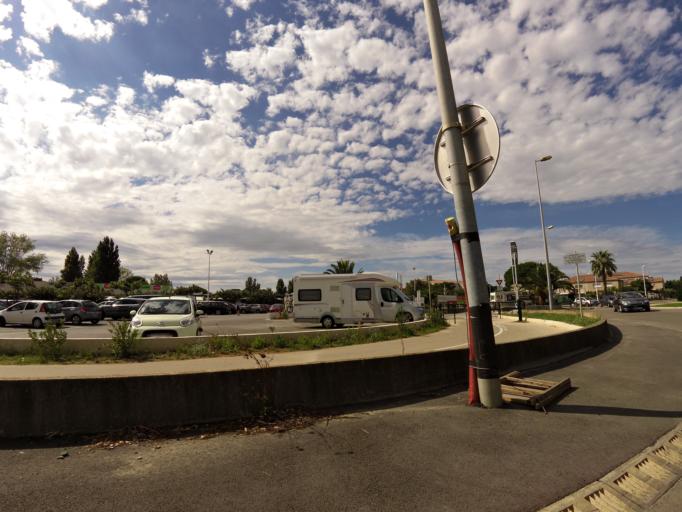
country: FR
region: Languedoc-Roussillon
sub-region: Departement du Gard
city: Le Grau-du-Roi
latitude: 43.5167
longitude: 4.1504
